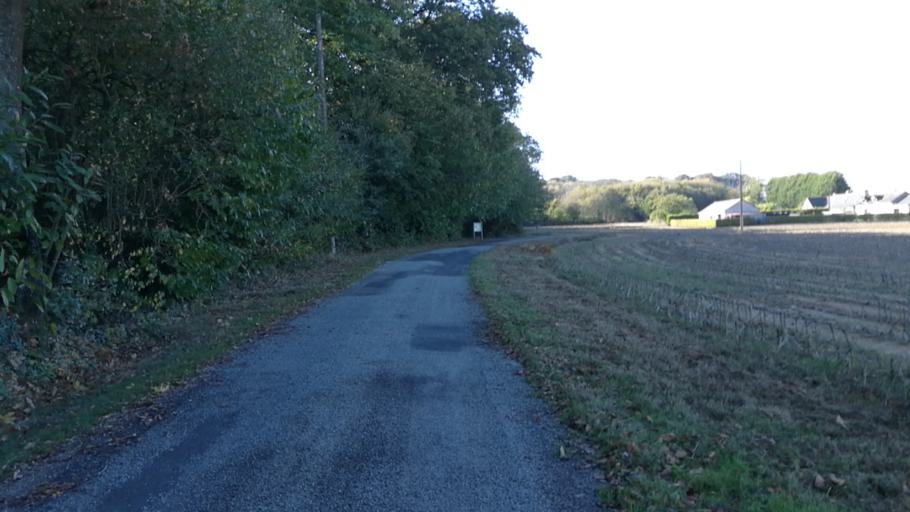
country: FR
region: Brittany
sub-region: Departement d'Ille-et-Vilaine
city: Retiers
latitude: 47.9128
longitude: -1.3979
